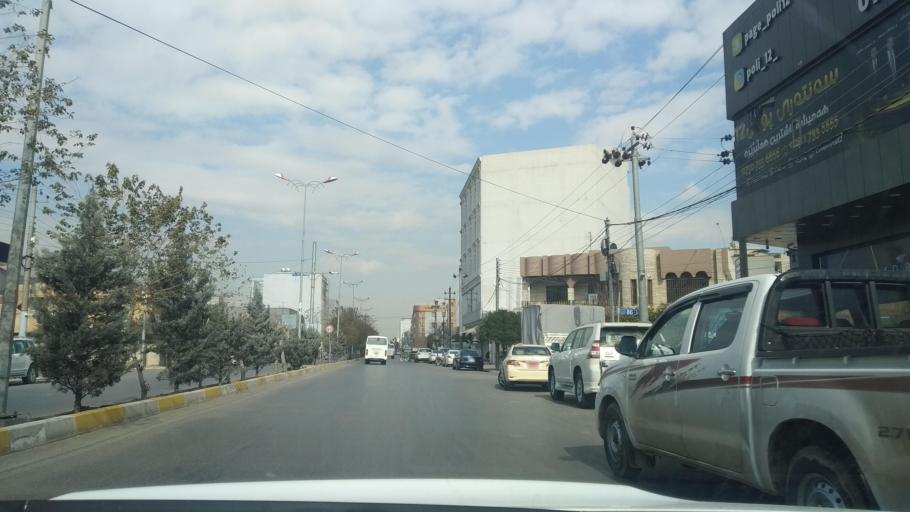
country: IQ
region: Arbil
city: Erbil
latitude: 36.1761
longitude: 44.0367
